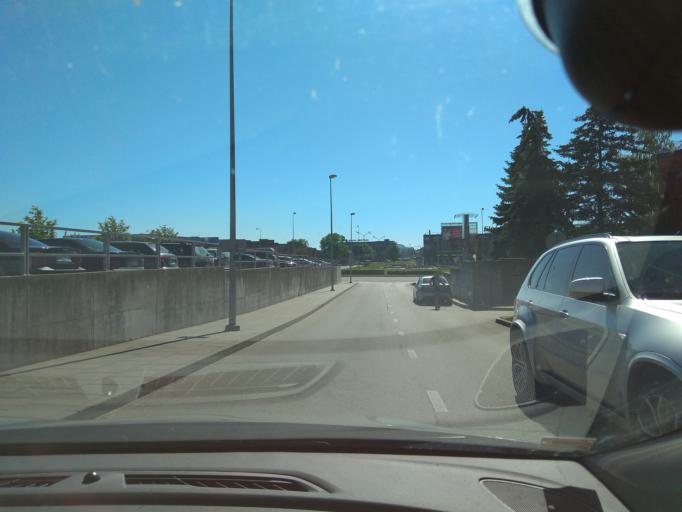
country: LT
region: Klaipedos apskritis
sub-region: Klaipeda
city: Klaipeda
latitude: 55.6911
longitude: 21.1556
